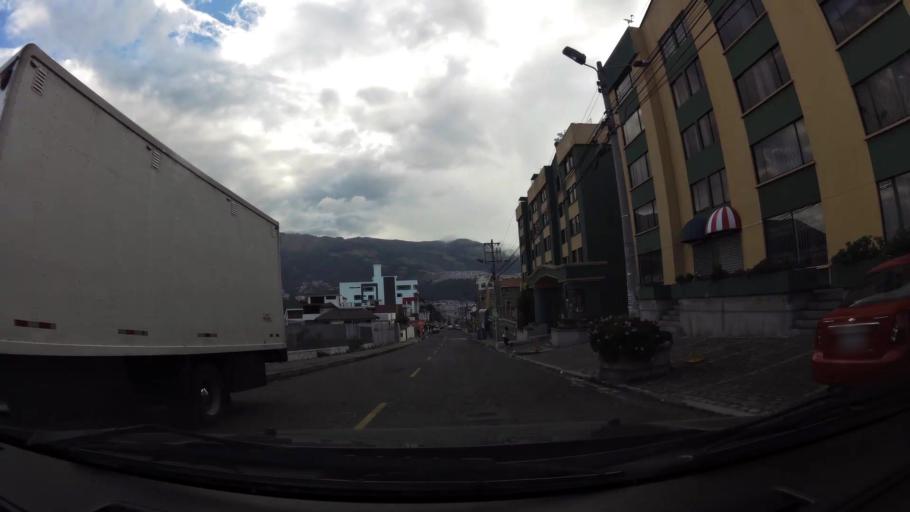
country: EC
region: Pichincha
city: Quito
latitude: -0.1312
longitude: -78.4767
